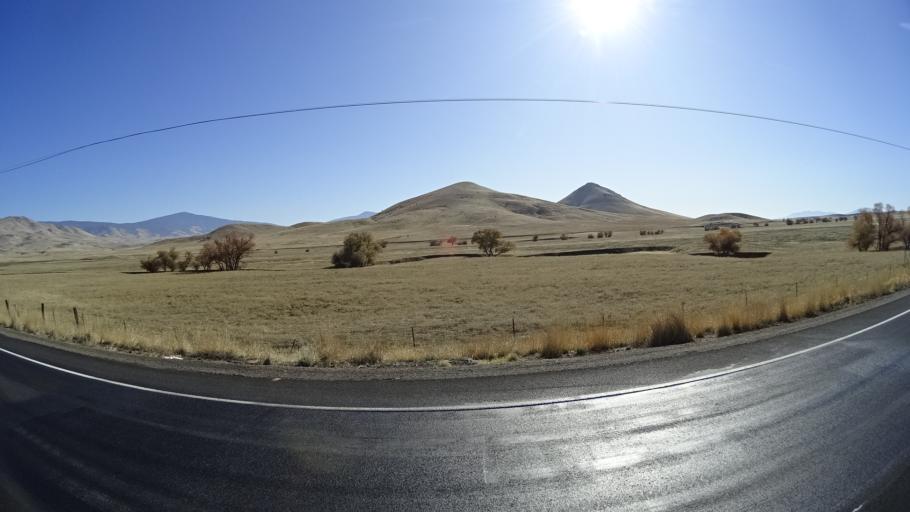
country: US
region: California
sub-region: Siskiyou County
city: Montague
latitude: 41.8359
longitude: -122.4846
